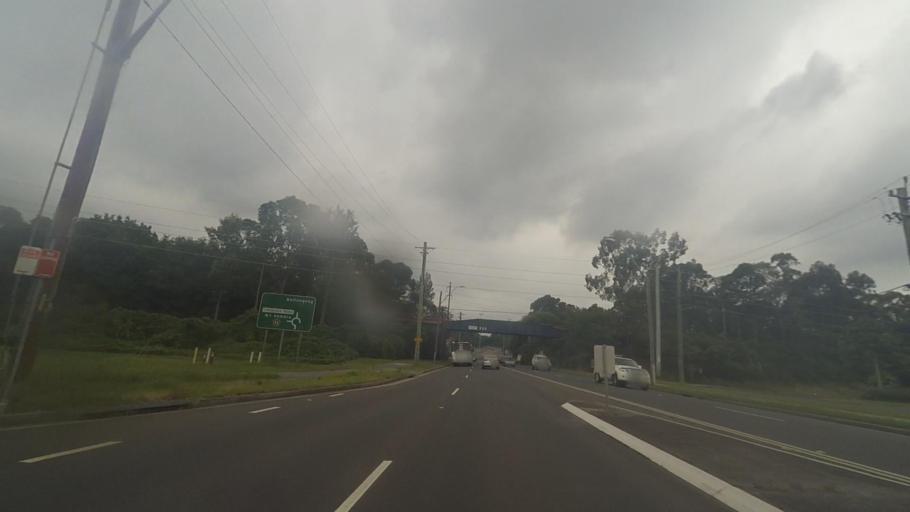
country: AU
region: New South Wales
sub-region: Wollongong
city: Cordeaux Heights
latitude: -34.4482
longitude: 150.8507
